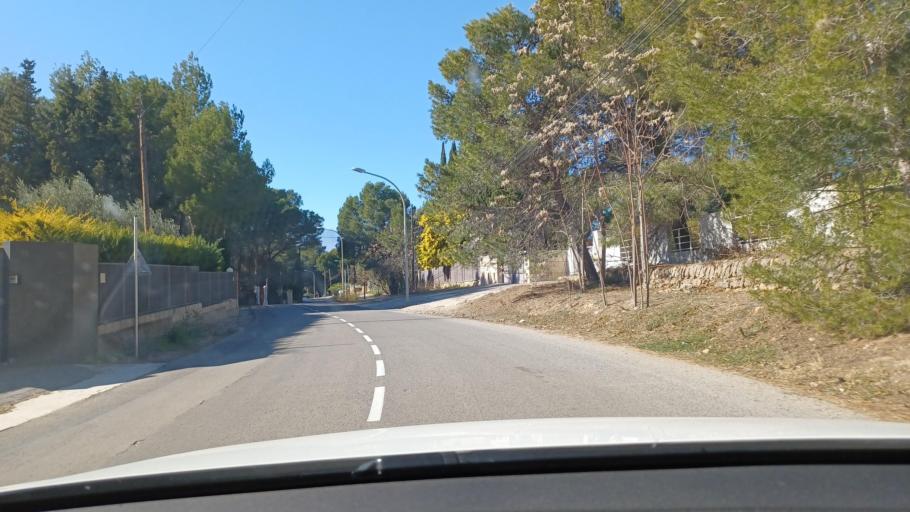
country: ES
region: Catalonia
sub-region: Provincia de Tarragona
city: Tortosa
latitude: 40.8133
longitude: 0.5388
